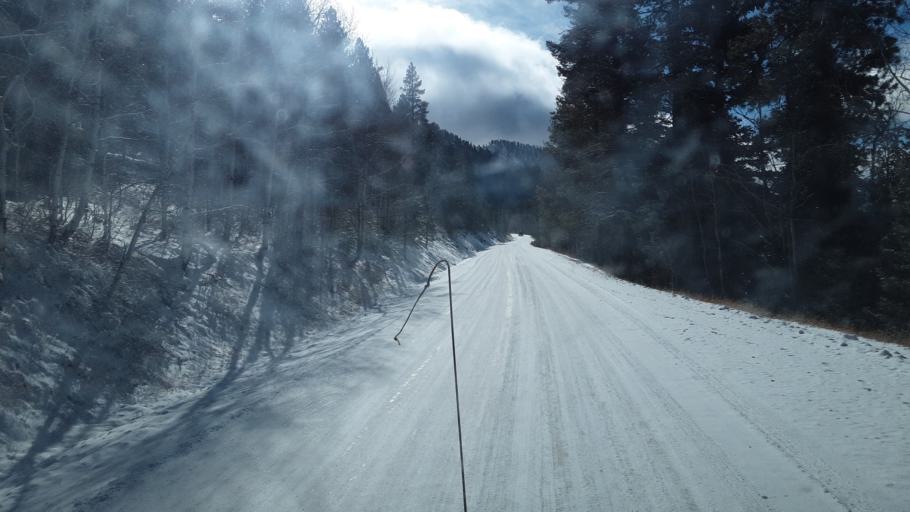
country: US
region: Colorado
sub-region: La Plata County
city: Bayfield
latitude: 37.3993
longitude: -107.6593
